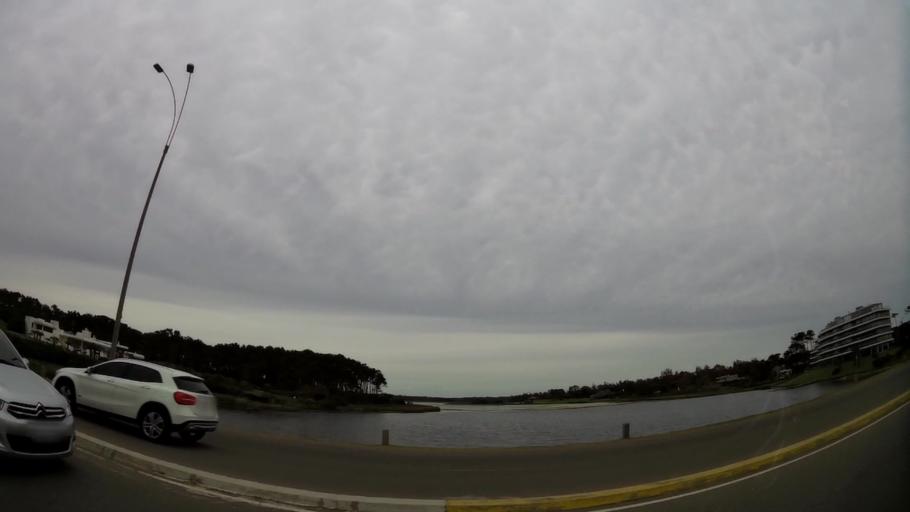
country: UY
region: Maldonado
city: Maldonado
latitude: -34.9092
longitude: -55.0075
